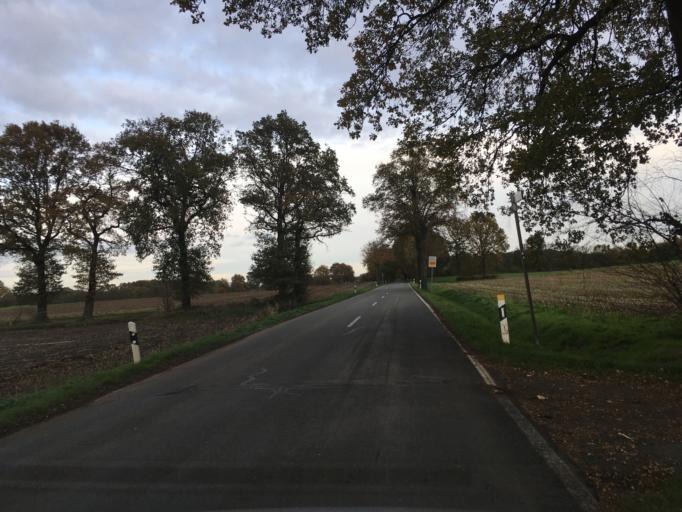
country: DE
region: North Rhine-Westphalia
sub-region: Regierungsbezirk Munster
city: Raesfeld
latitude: 51.7383
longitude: 6.8194
